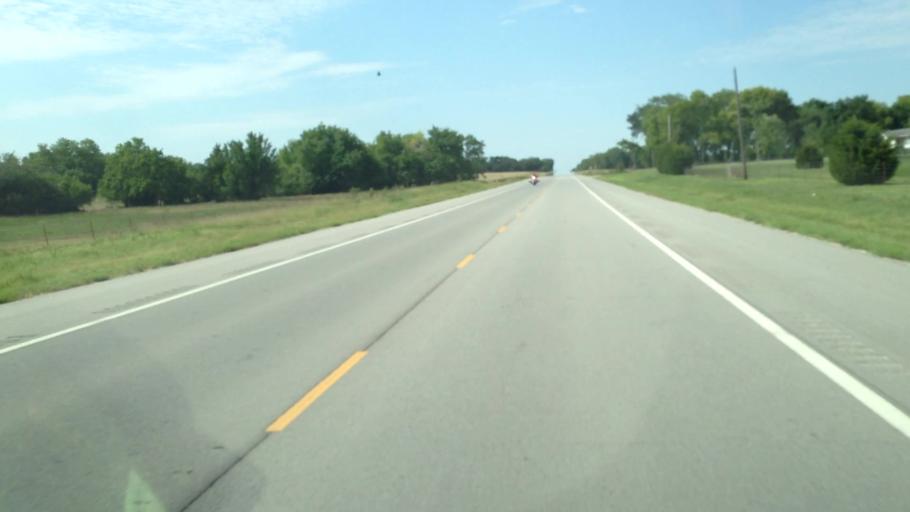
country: US
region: Kansas
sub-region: Labette County
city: Parsons
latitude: 37.2974
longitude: -95.2675
